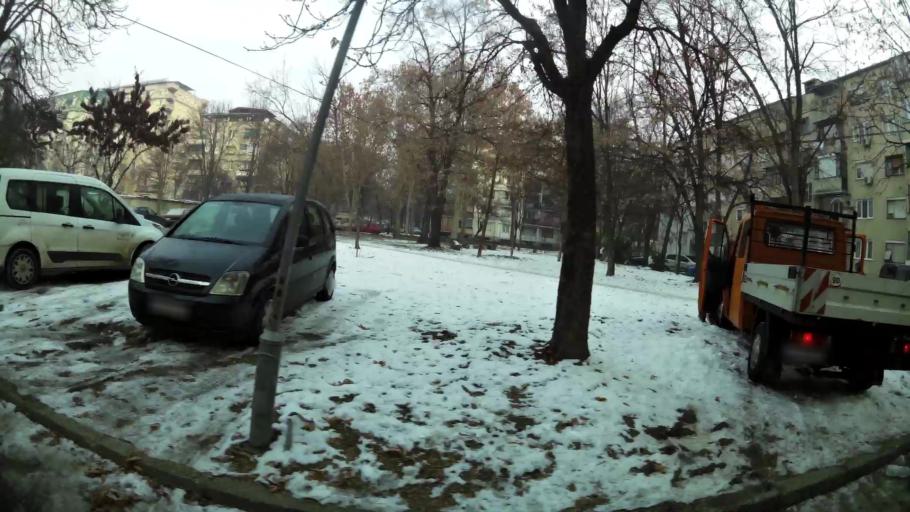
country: MK
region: Cair
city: Cair
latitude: 42.0166
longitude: 21.4463
